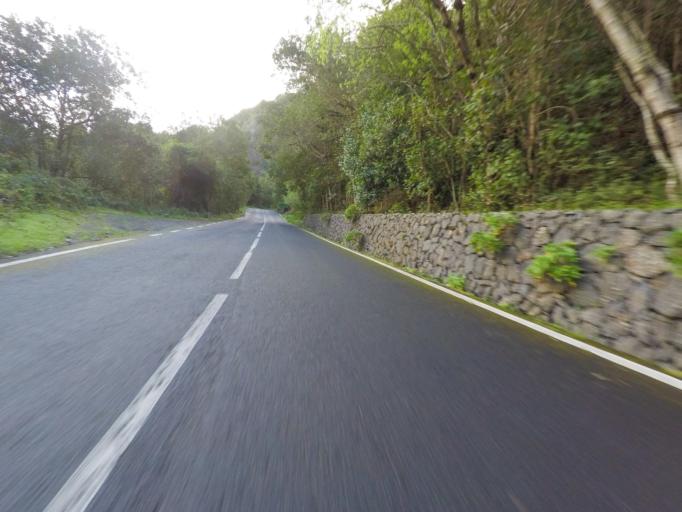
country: ES
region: Canary Islands
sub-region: Provincia de Santa Cruz de Tenerife
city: Hermigua
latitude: 28.1252
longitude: -17.2111
